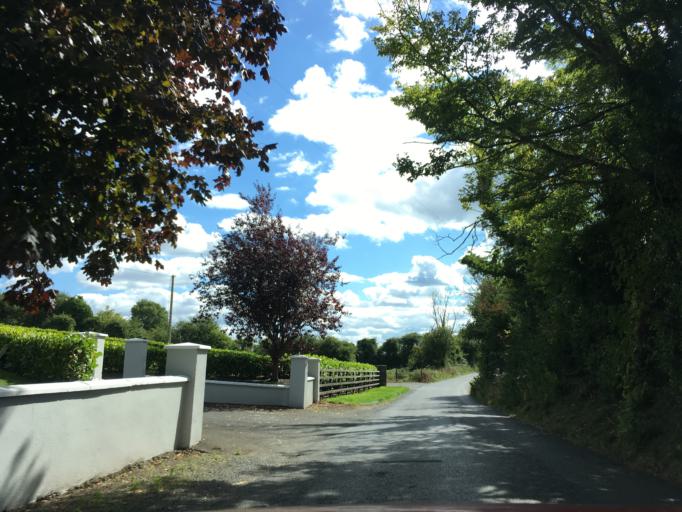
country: IE
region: Munster
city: Cashel
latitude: 52.5029
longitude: -7.8968
